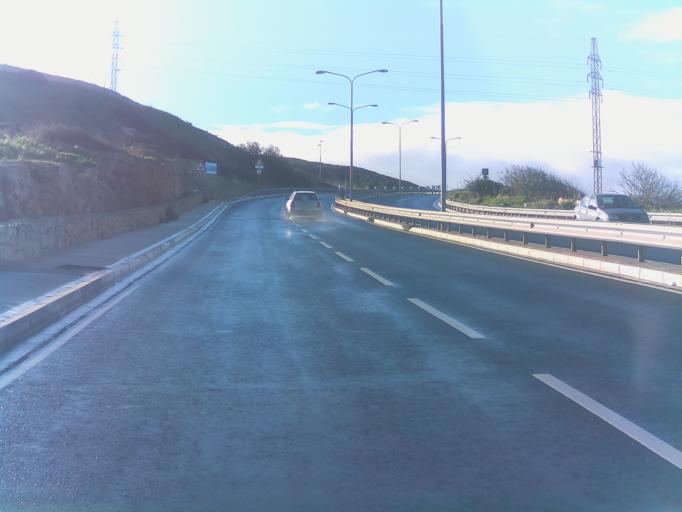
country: MT
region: Il-Mellieha
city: Mellieha
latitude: 35.9589
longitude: 14.3510
